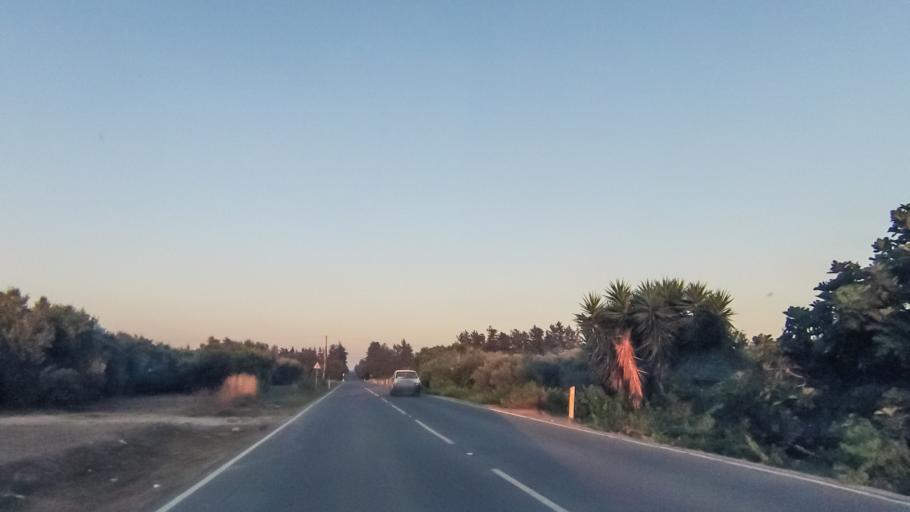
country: CY
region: Limassol
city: Erimi
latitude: 34.6612
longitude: 32.9002
